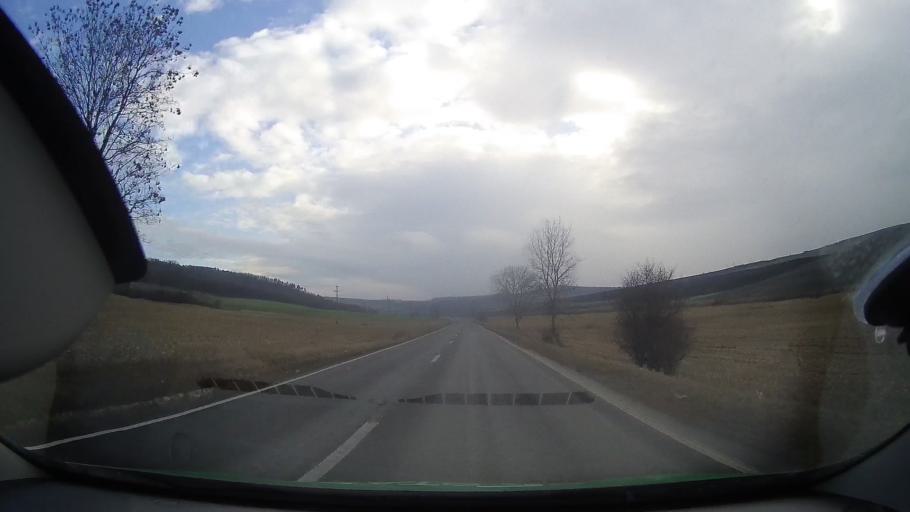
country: RO
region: Mures
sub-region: Comuna Cucerdea
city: Cucerdea
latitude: 46.3752
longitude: 24.2578
